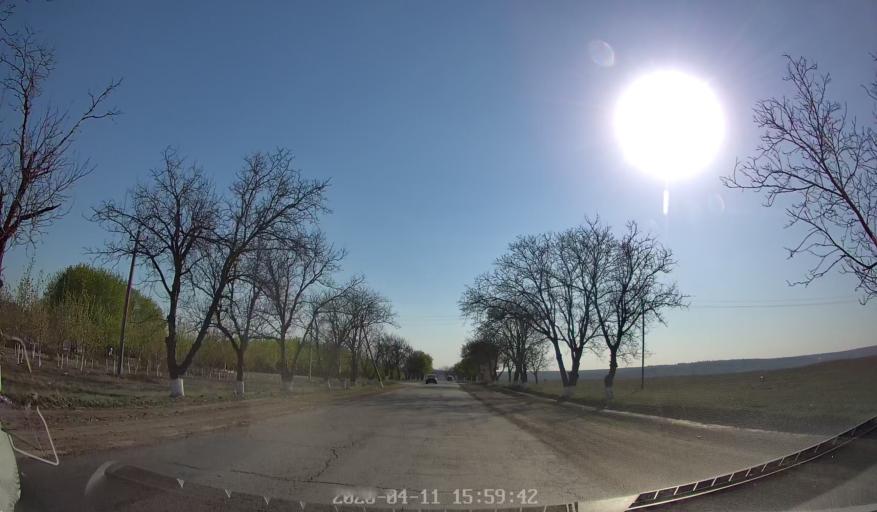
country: MD
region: Chisinau
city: Vadul lui Voda
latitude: 47.0804
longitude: 29.1392
